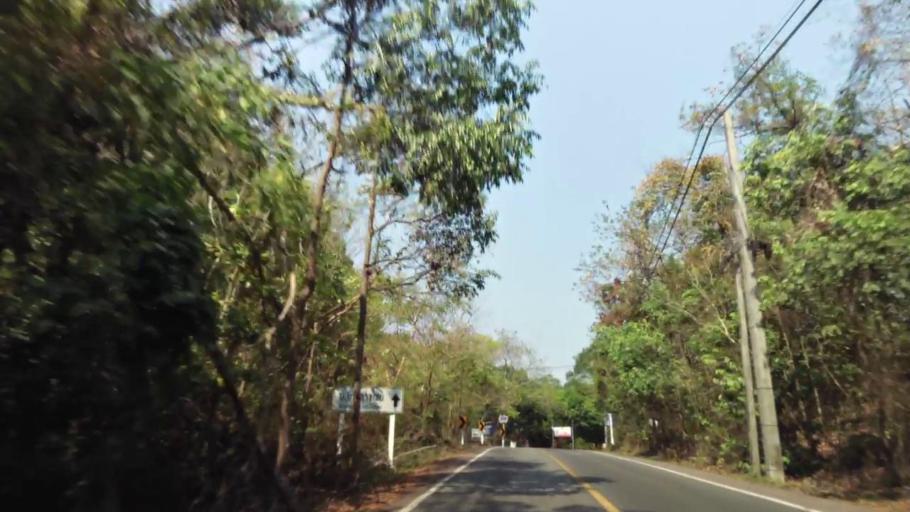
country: TH
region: Chanthaburi
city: Tha Mai
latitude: 12.5378
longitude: 101.9468
